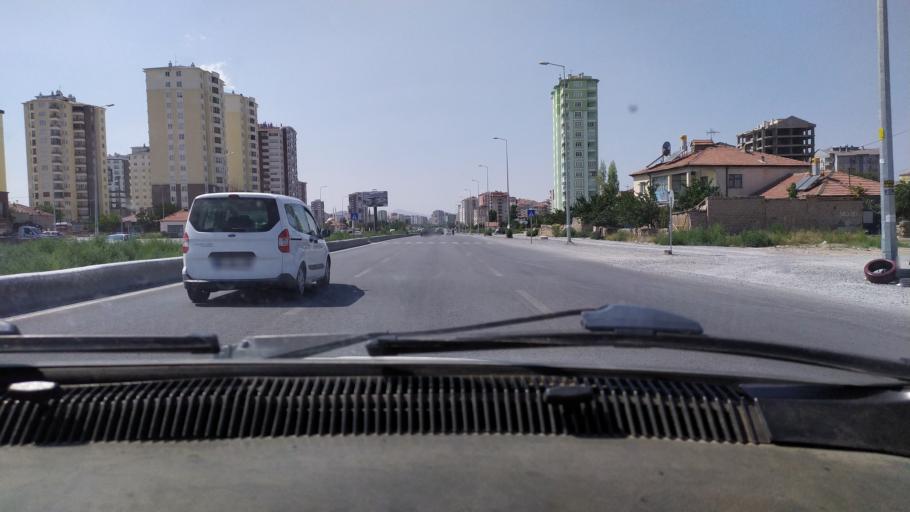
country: TR
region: Kayseri
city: Talas
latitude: 38.7206
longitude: 35.5437
